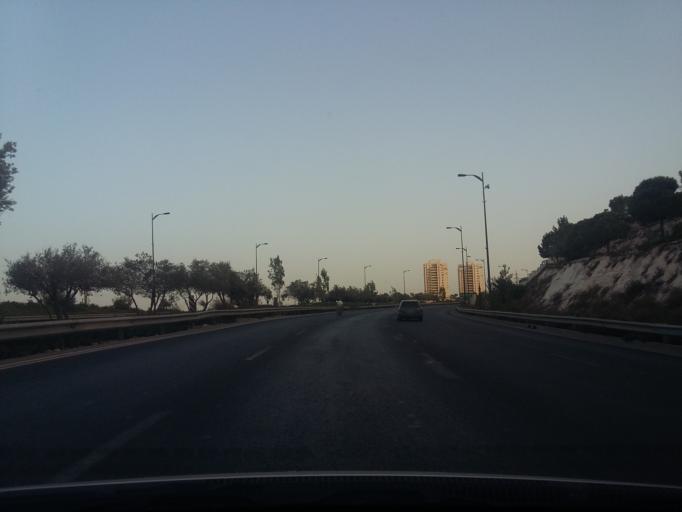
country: PS
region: West Bank
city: `Anata
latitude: 31.8139
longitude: 35.2385
